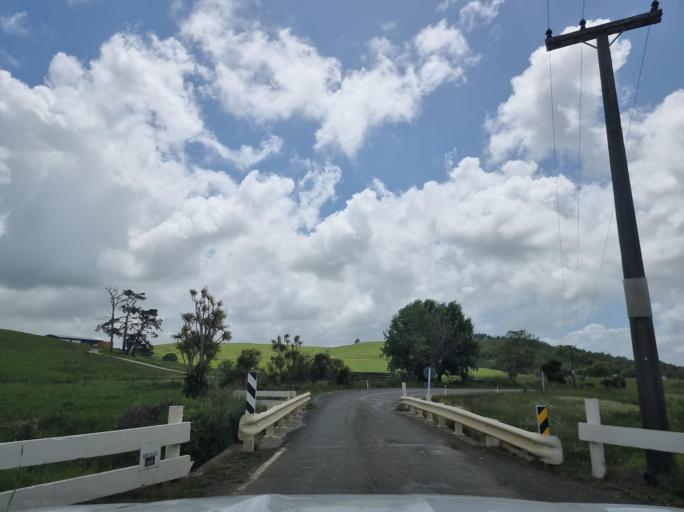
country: NZ
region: Northland
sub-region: Kaipara District
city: Dargaville
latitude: -36.1120
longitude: 174.1317
